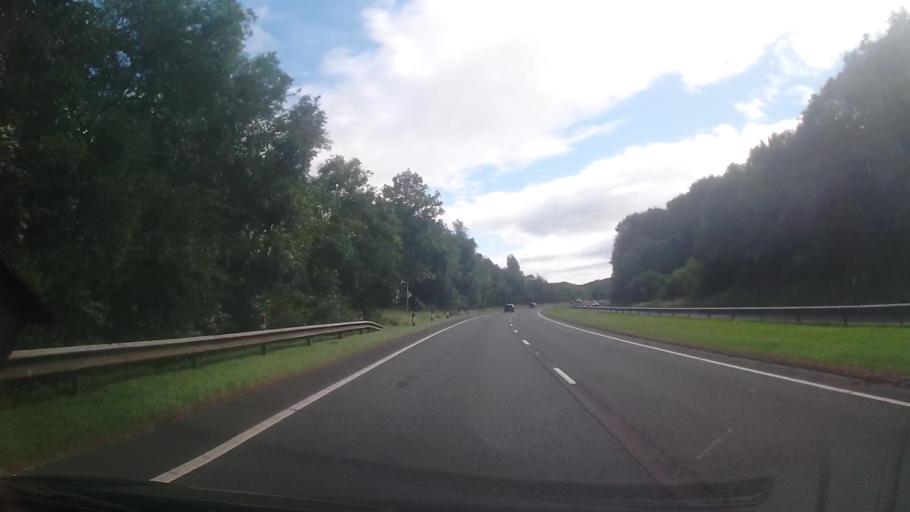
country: GB
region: Wales
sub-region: Wrexham
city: Gresford
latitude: 53.0896
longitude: -2.9844
